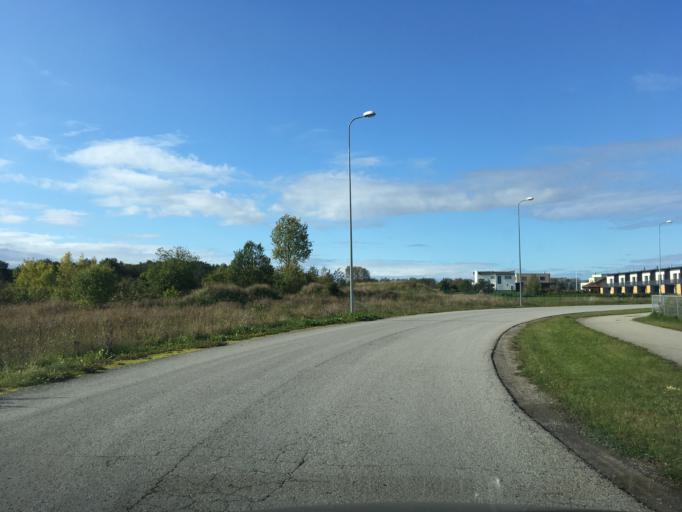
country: EE
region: Harju
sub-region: Saue vald
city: Laagri
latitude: 59.3453
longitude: 24.6443
